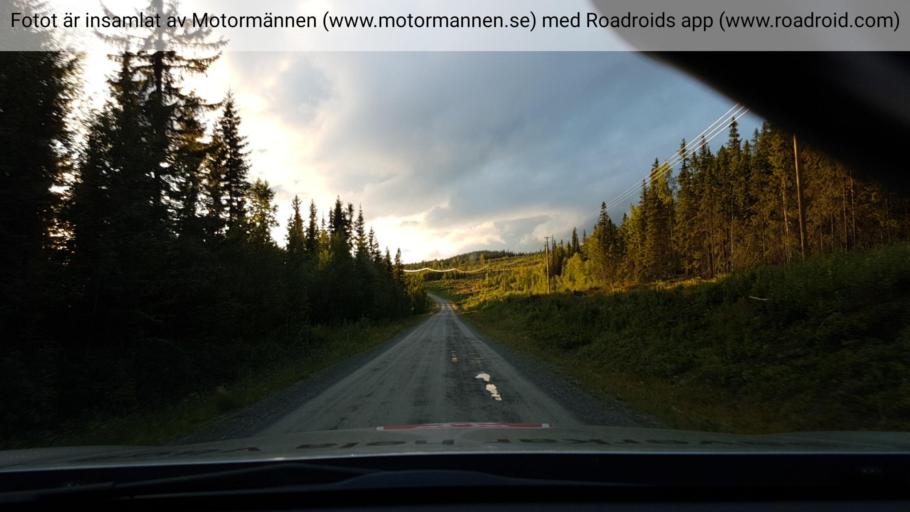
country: SE
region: Vaesterbotten
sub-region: Vilhelmina Kommun
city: Sjoberg
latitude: 65.5592
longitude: 15.3948
